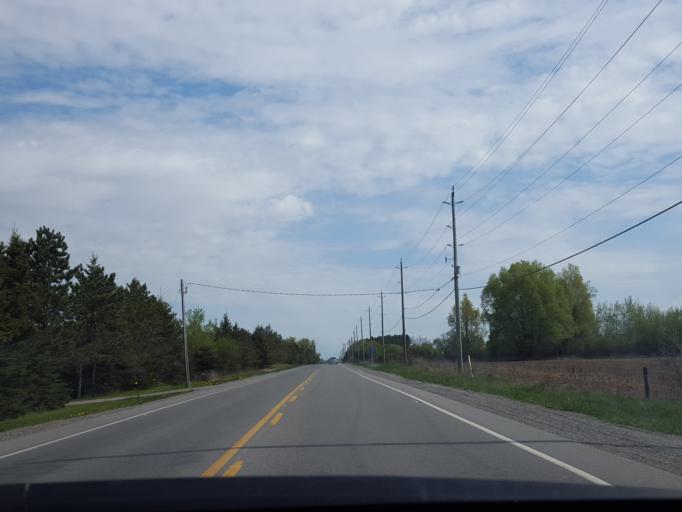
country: CA
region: Ontario
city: Uxbridge
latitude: 44.1568
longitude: -78.8989
